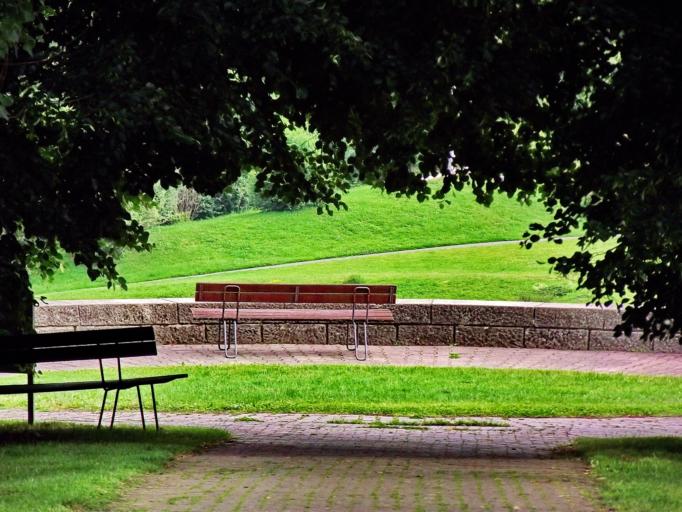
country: DE
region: Baden-Wuerttemberg
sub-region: Regierungsbezirk Stuttgart
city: Ostfildern
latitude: 48.7094
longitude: 9.2147
